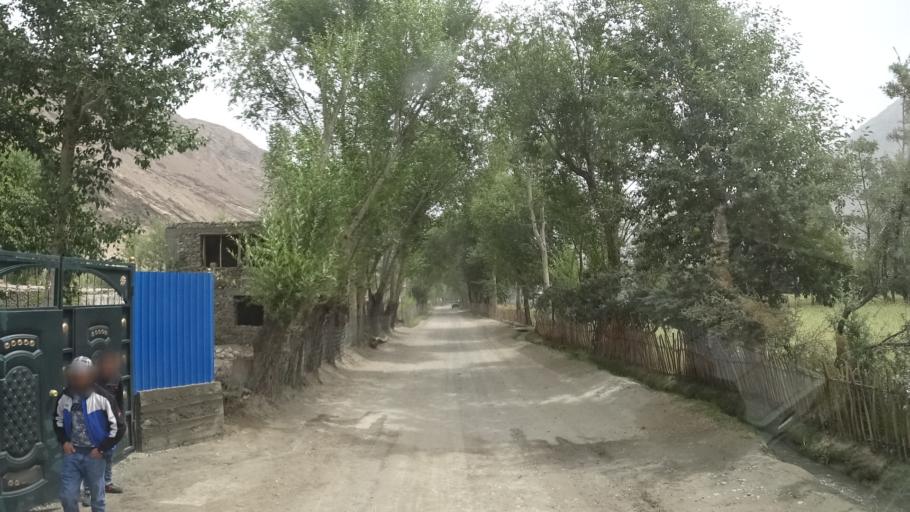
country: AF
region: Badakhshan
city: Khandud
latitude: 37.0220
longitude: 72.5904
